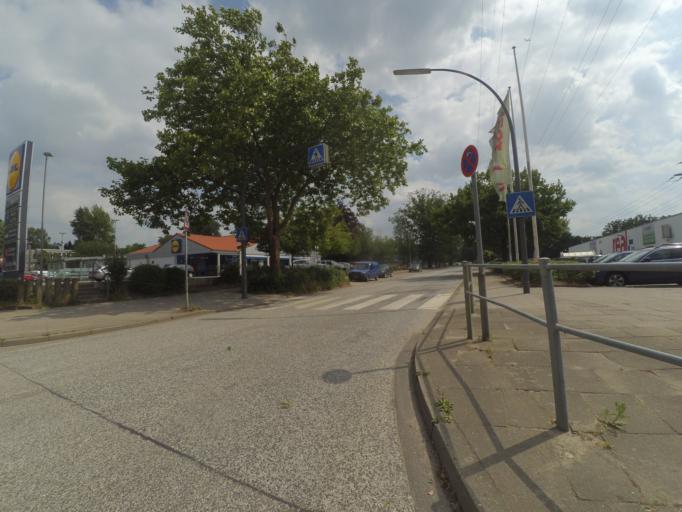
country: DE
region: Hamburg
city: Eidelstedt
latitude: 53.5849
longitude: 9.8721
